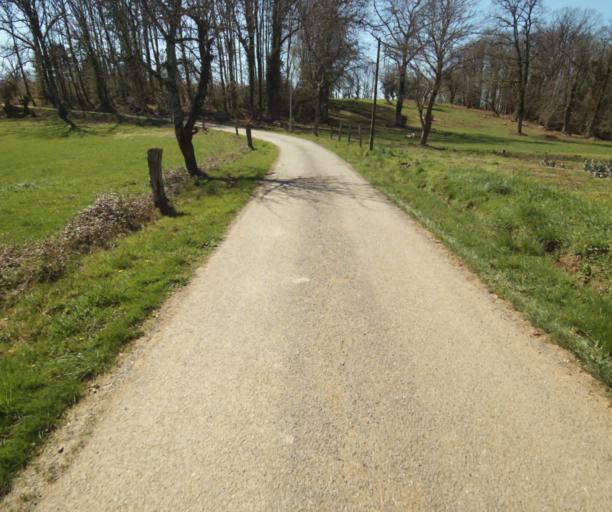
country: FR
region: Limousin
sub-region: Departement de la Correze
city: Chamboulive
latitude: 45.3978
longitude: 1.6803
